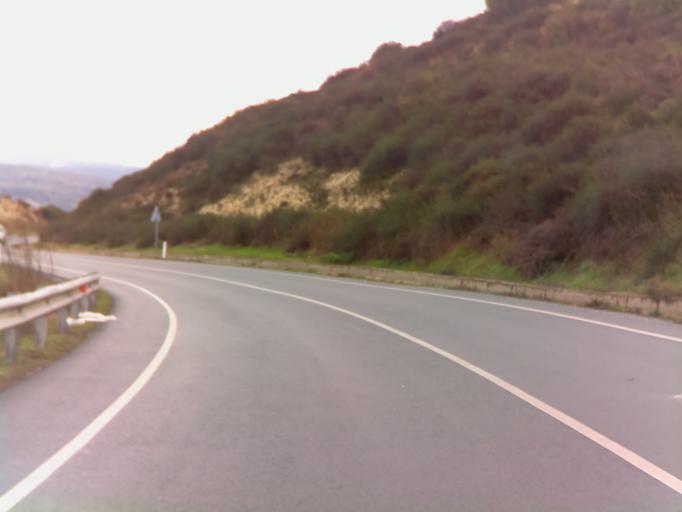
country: CY
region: Pafos
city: Tala
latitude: 34.8994
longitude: 32.4478
